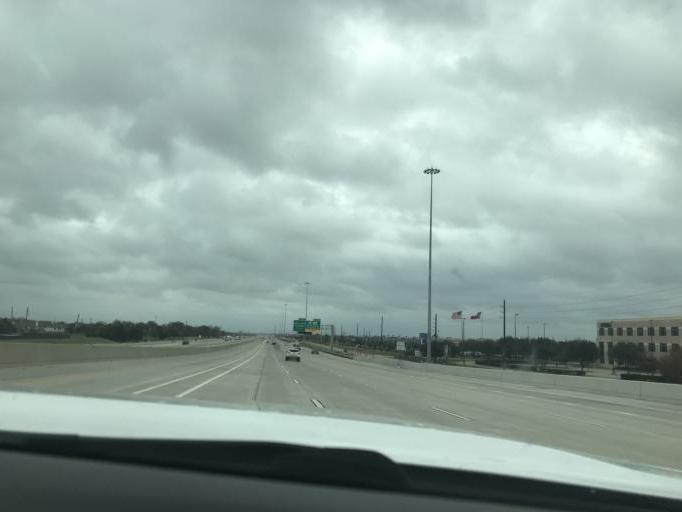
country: US
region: Texas
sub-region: Fort Bend County
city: Greatwood
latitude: 29.5563
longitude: -95.7147
